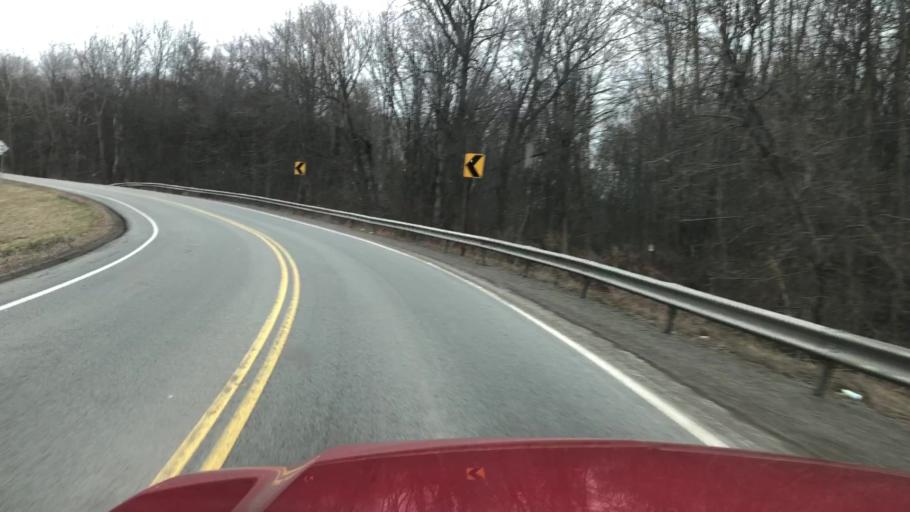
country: US
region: New York
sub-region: Monroe County
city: Fairport
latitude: 43.1300
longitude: -77.3722
